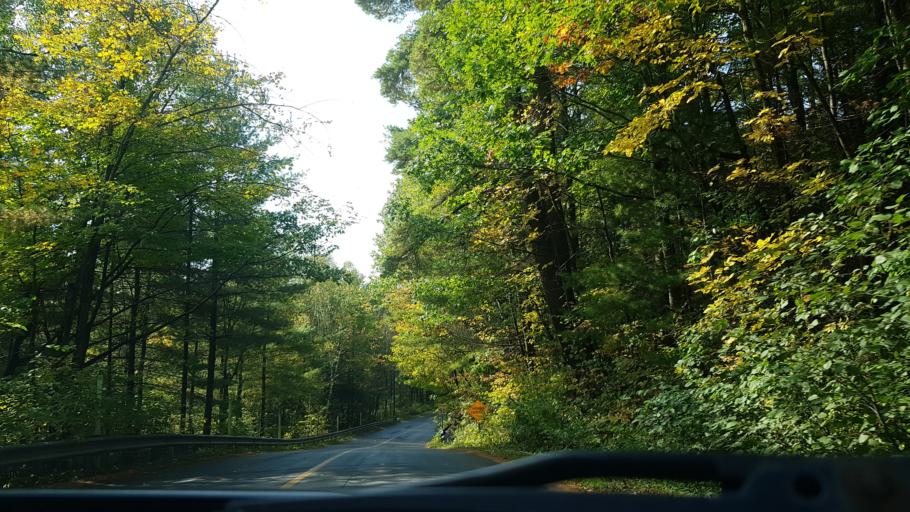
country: CA
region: Ontario
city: Gravenhurst
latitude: 44.7950
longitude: -79.2087
